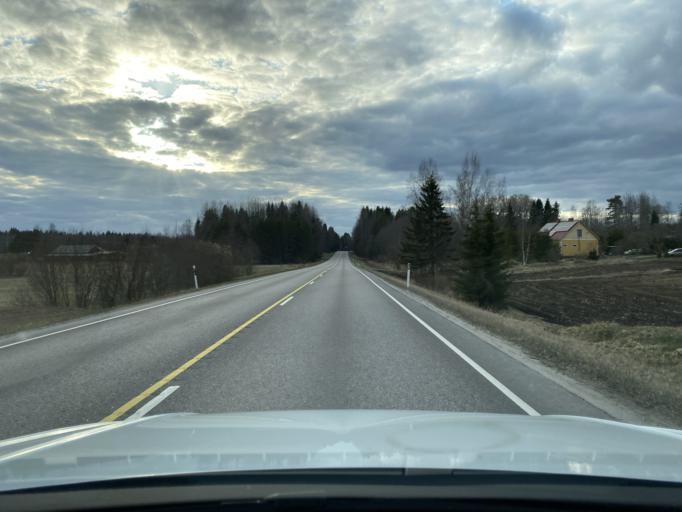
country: FI
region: Haeme
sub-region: Haemeenlinna
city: Renko
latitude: 60.7902
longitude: 24.1235
